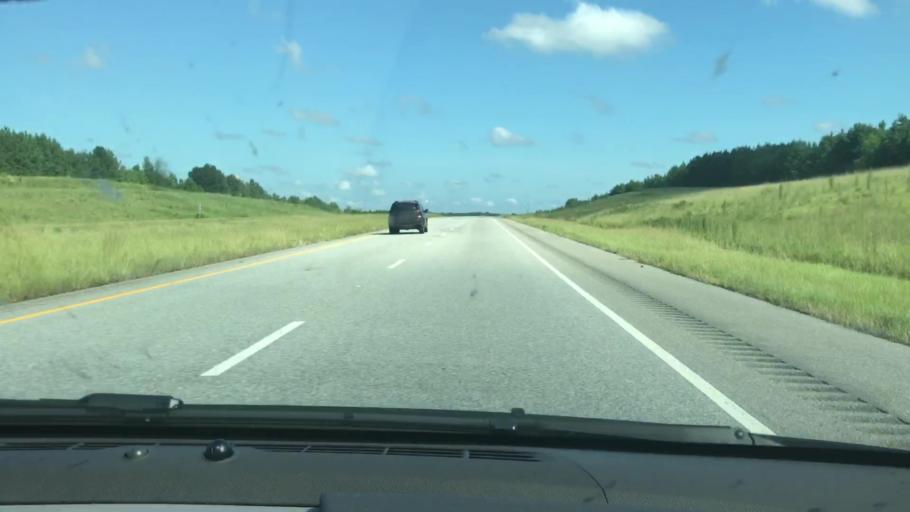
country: US
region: Alabama
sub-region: Barbour County
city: Eufaula
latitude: 32.1747
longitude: -85.1770
